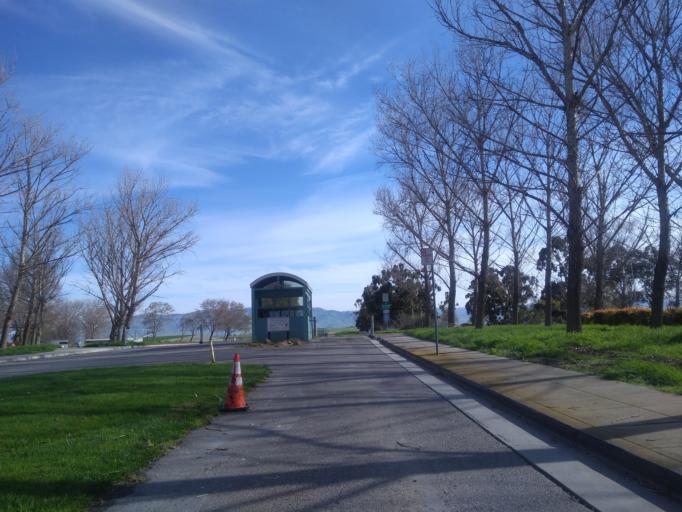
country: US
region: California
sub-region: Santa Clara County
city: Sunnyvale
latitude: 37.4121
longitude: -121.9998
